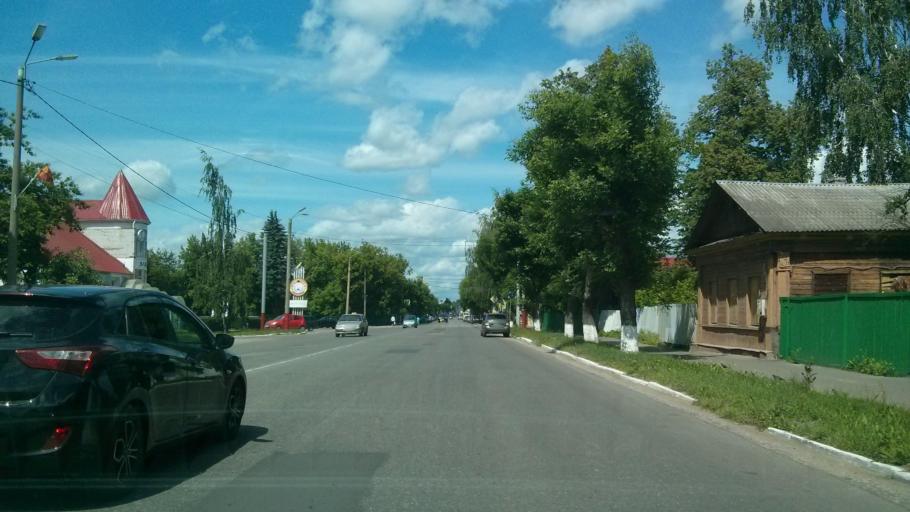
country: RU
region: Vladimir
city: Murom
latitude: 55.5744
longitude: 42.0559
